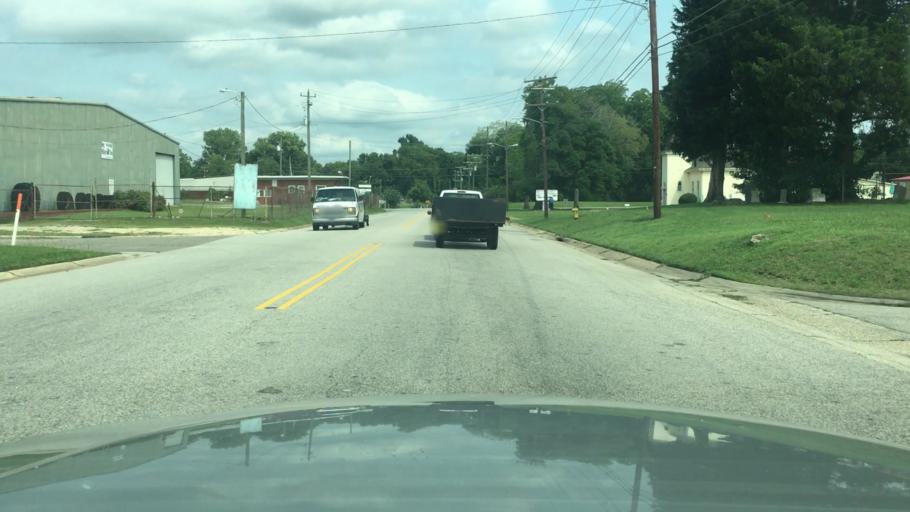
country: US
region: North Carolina
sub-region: Cumberland County
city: Fayetteville
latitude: 35.0456
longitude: -78.8645
